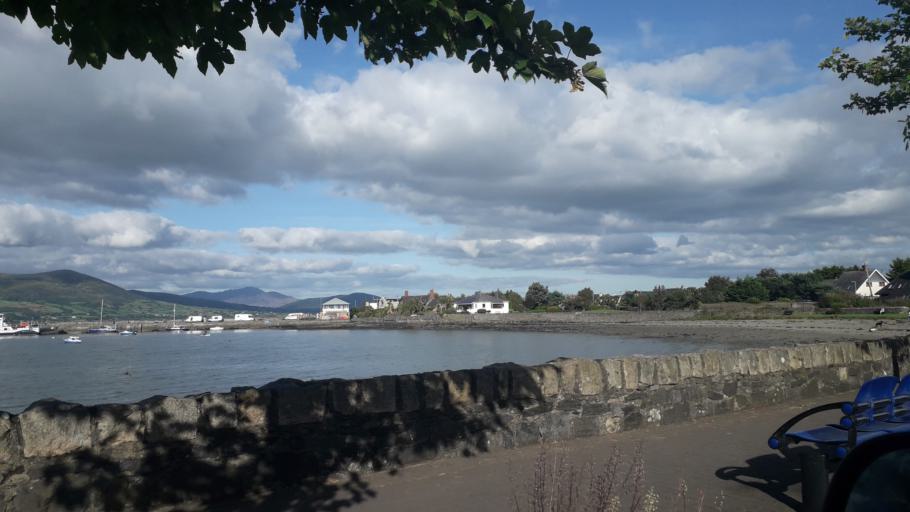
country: IE
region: Leinster
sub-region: Lu
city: Carlingford
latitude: 54.0404
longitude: -6.1841
